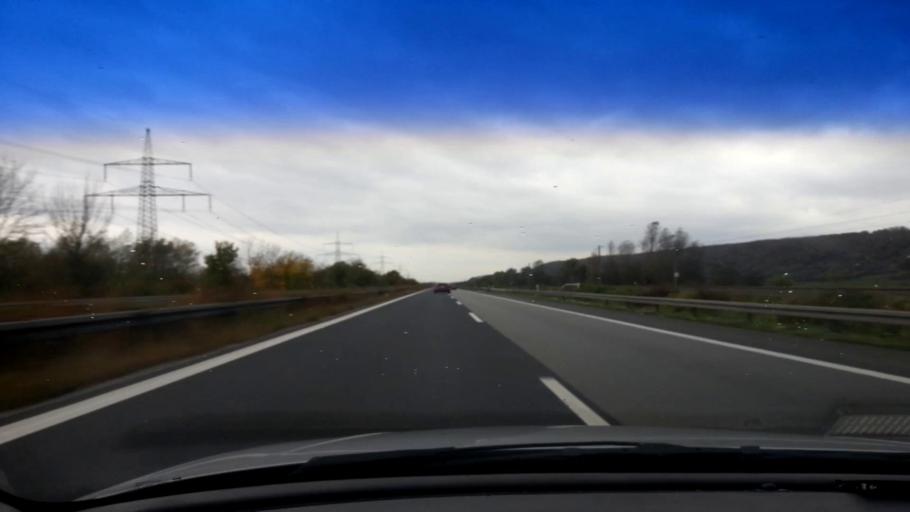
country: DE
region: Bavaria
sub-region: Regierungsbezirk Unterfranken
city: Stettfeld
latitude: 49.9684
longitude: 10.7138
